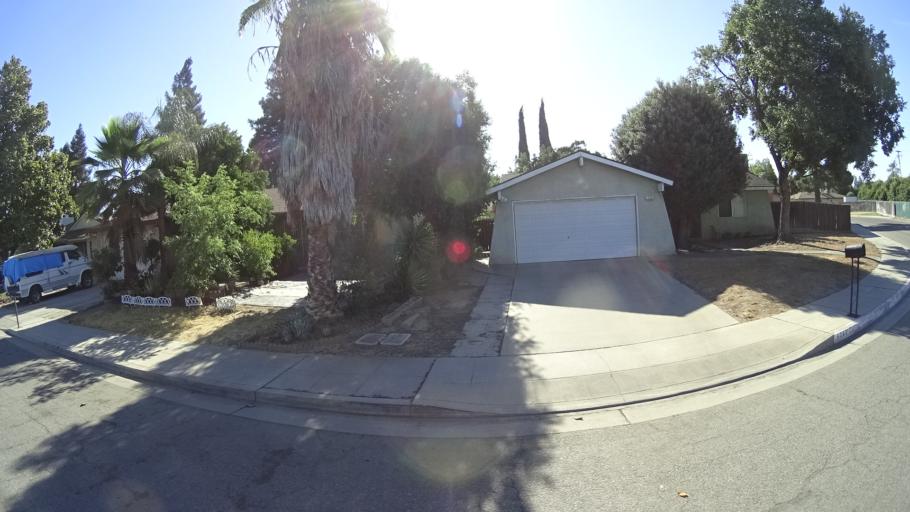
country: US
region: California
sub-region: Fresno County
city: West Park
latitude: 36.7801
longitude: -119.8687
